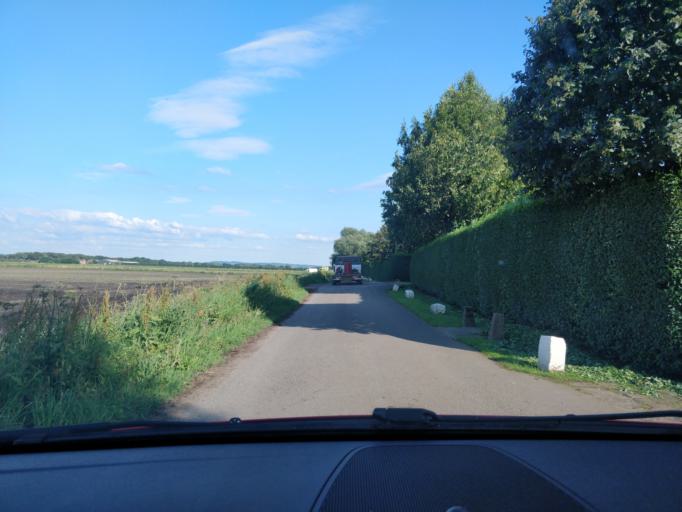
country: GB
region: England
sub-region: Lancashire
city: Banks
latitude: 53.6549
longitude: -2.9236
